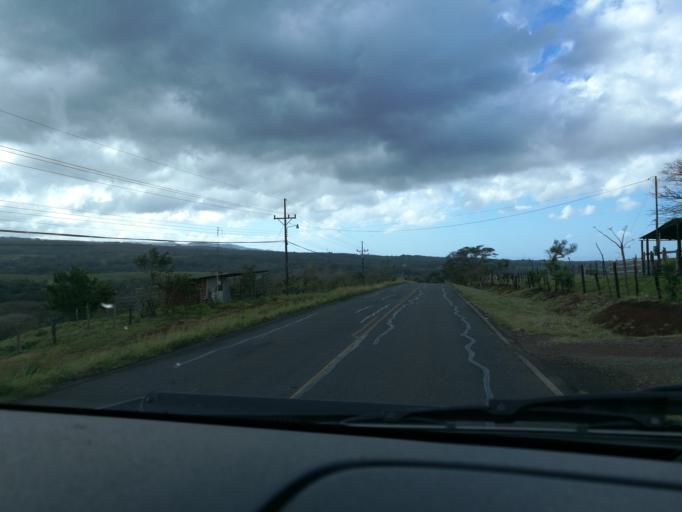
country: CR
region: Alajuela
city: Bijagua
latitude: 10.6692
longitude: -85.0901
